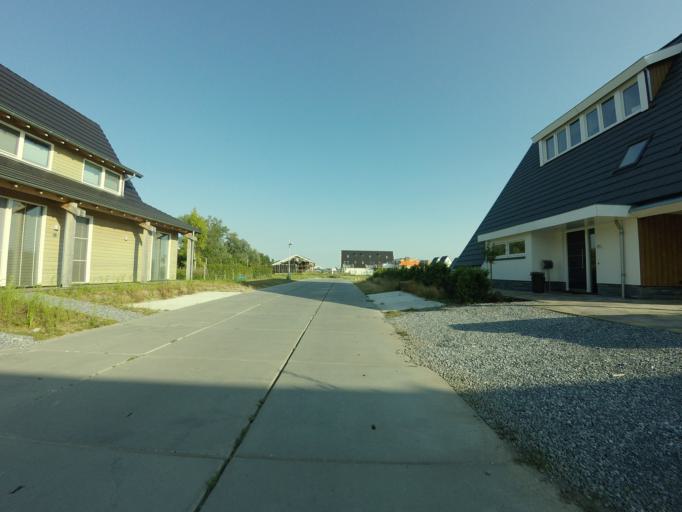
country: NL
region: South Holland
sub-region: Gemeente Nieuwkoop
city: Nieuwkoop
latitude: 52.1334
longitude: 4.7695
